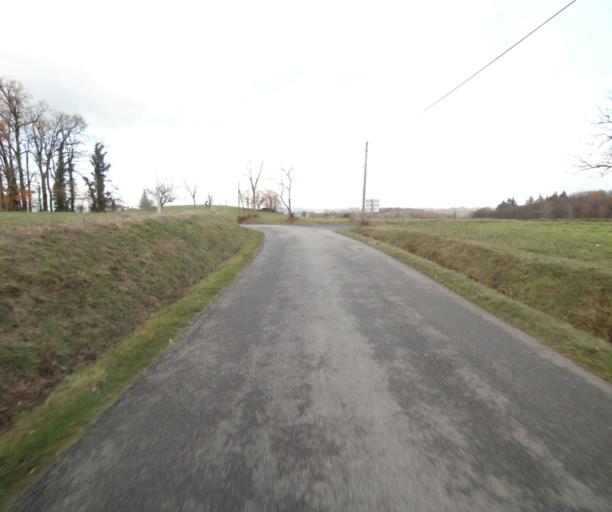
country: FR
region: Limousin
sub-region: Departement de la Correze
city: Sainte-Fortunade
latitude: 45.2122
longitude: 1.7889
